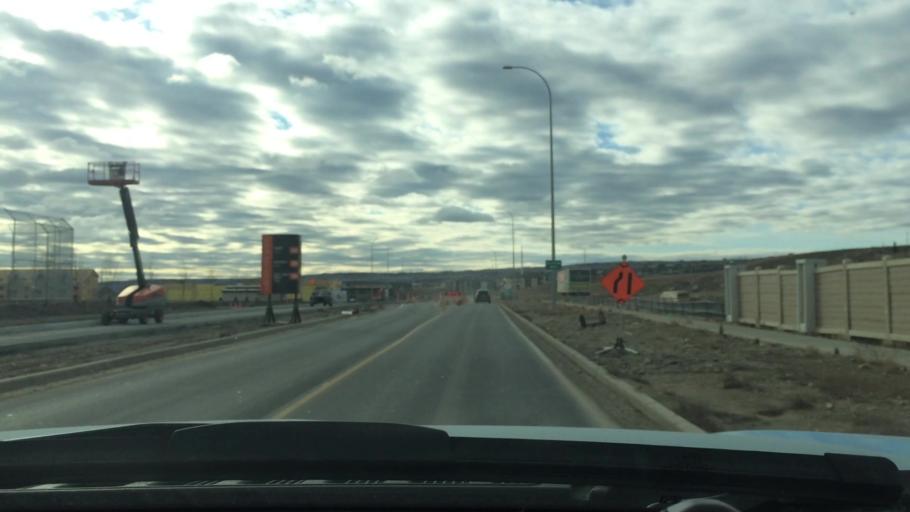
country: CA
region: Alberta
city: Calgary
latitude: 51.1777
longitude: -114.1335
